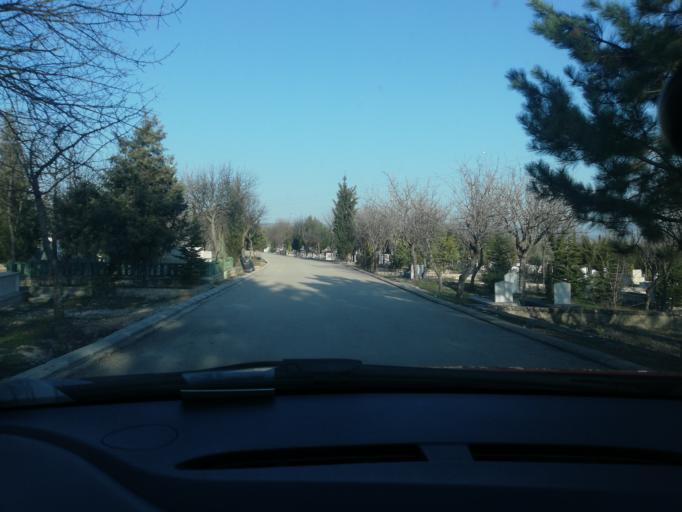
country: TR
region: Karabuk
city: Safranbolu
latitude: 41.2399
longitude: 32.6956
